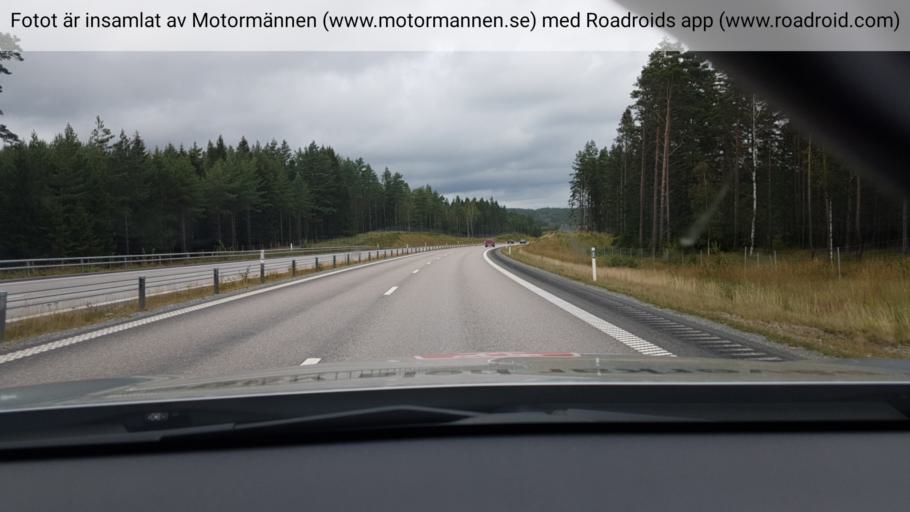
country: SE
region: Vaestra Goetaland
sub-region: Tanums Kommun
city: Tanumshede
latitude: 58.6763
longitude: 11.4089
